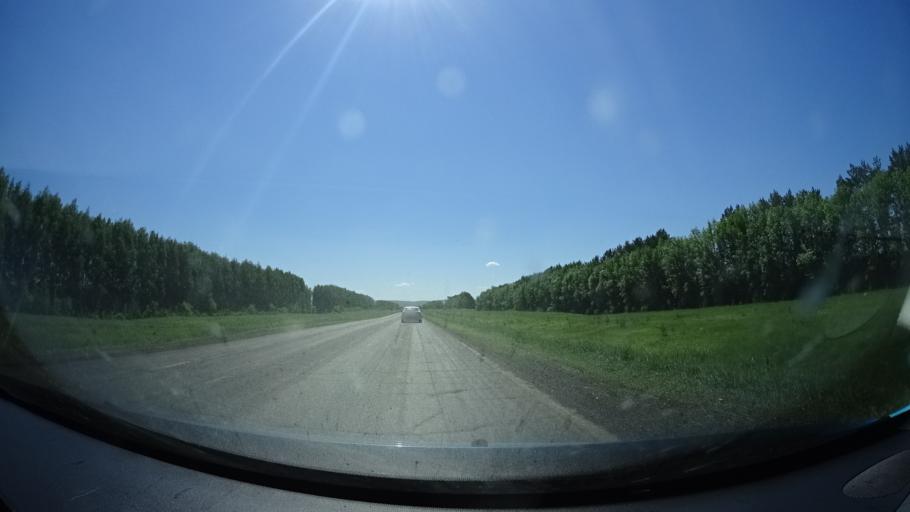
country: RU
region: Bashkortostan
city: Blagoveshchensk
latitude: 55.2331
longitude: 55.7800
